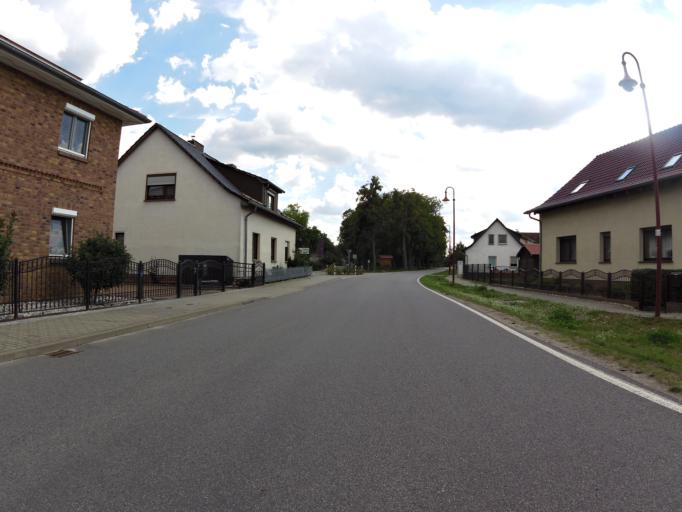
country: DE
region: Brandenburg
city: Munchehofe
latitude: 52.2165
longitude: 13.8730
